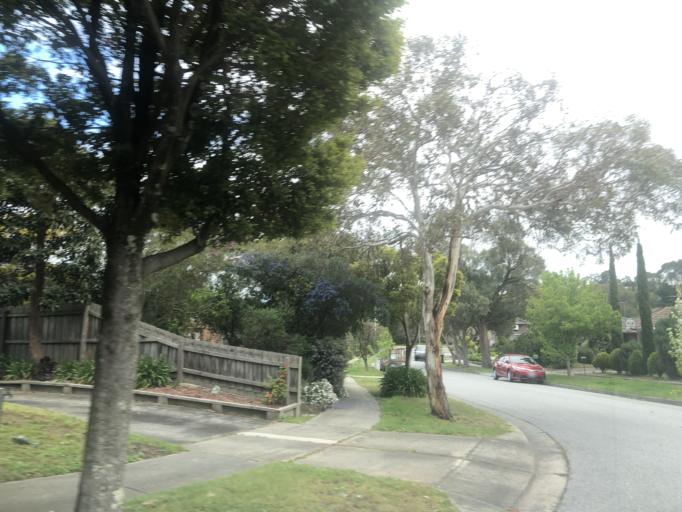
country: AU
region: Victoria
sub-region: Casey
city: Endeavour Hills
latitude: -37.9712
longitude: 145.2457
